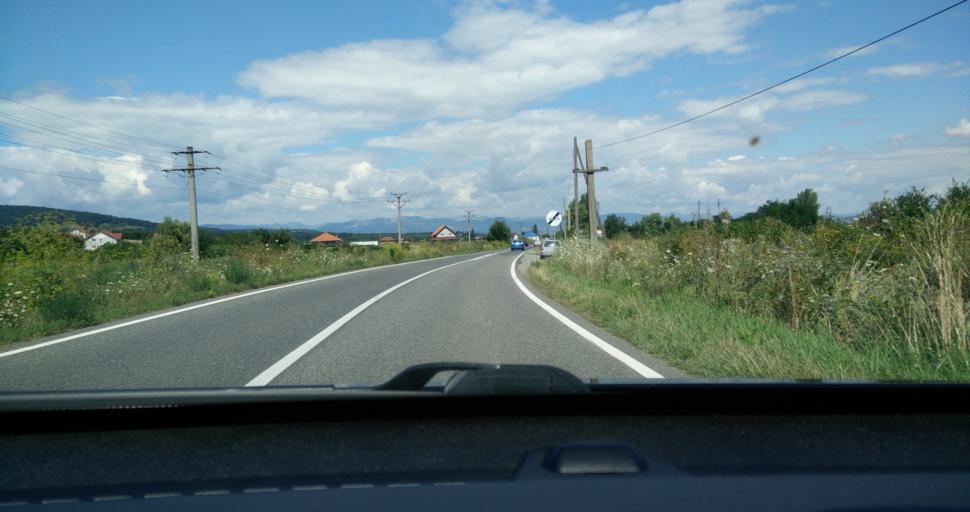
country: RO
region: Alba
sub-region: Comuna Sasciori
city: Sebesel
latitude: 45.9011
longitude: 23.5582
